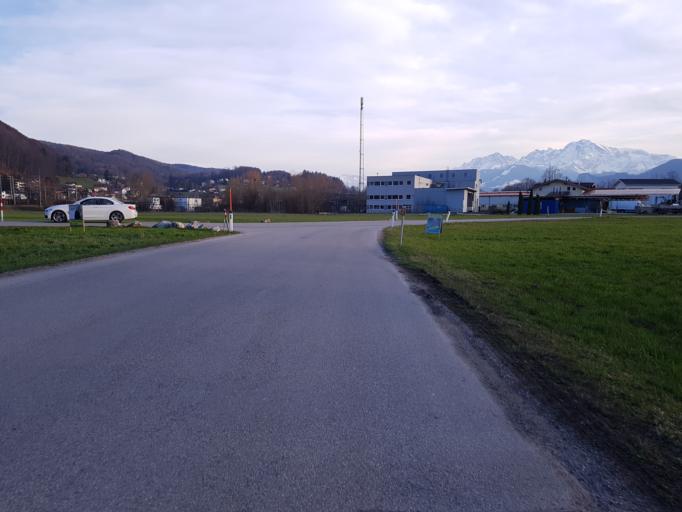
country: AT
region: Salzburg
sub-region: Politischer Bezirk Salzburg-Umgebung
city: Elsbethen
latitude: 47.7542
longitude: 13.0816
